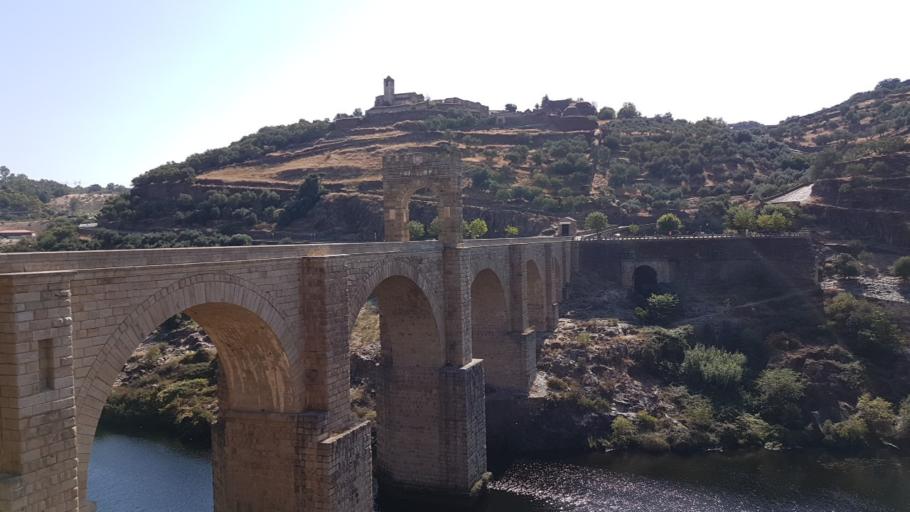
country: ES
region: Extremadura
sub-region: Provincia de Caceres
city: Alcantara
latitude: 39.7228
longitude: -6.8936
